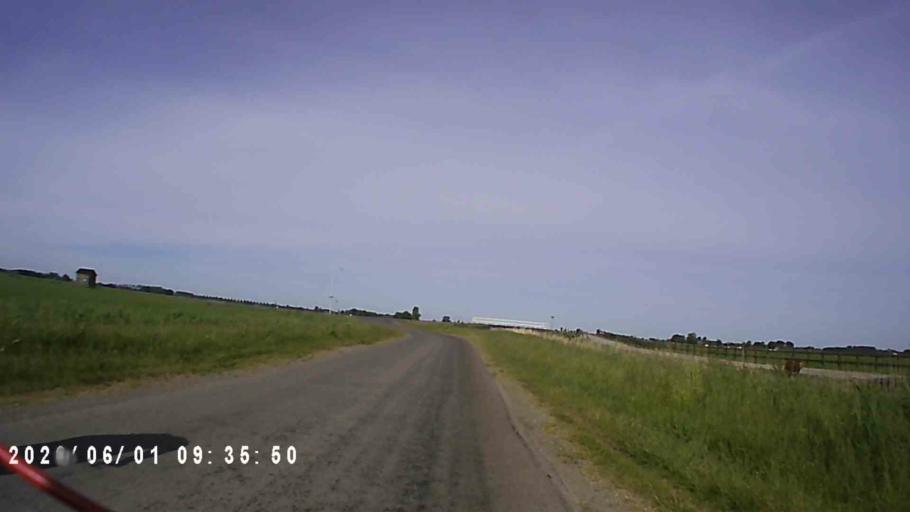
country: NL
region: Friesland
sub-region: Gemeente Het Bildt
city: Sint Annaparochie
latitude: 53.2596
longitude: 5.7029
